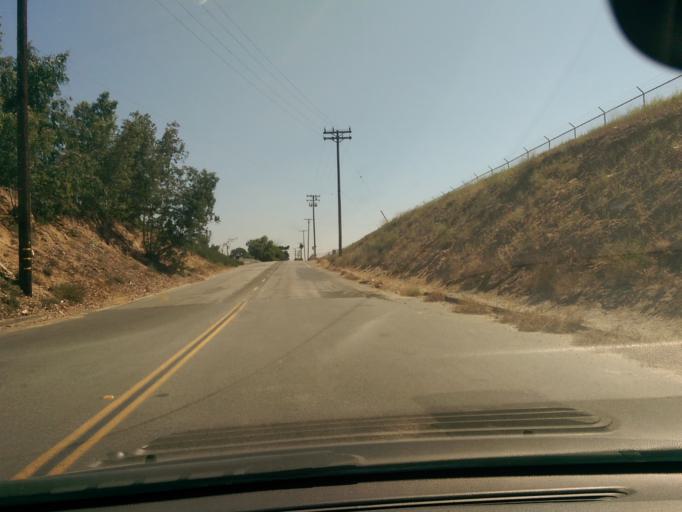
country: US
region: California
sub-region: Riverside County
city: Norco
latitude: 33.9196
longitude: -117.5939
